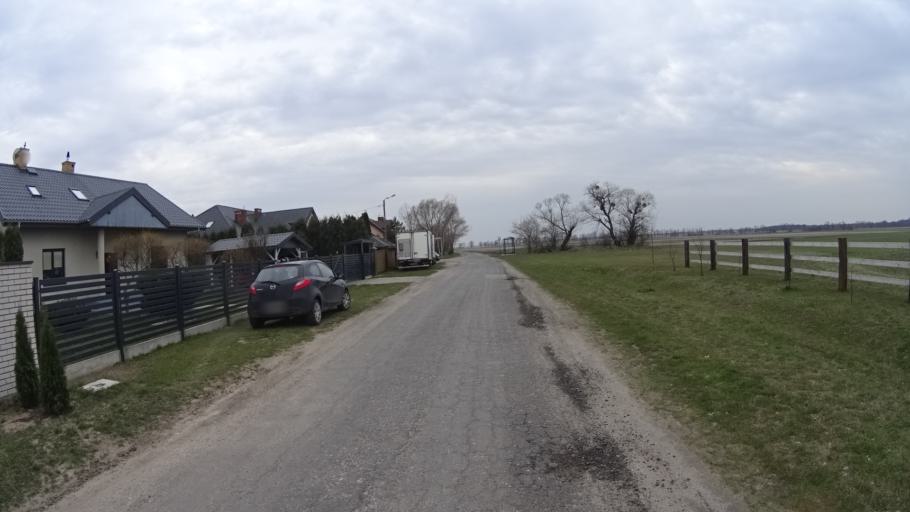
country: PL
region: Masovian Voivodeship
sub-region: Powiat warszawski zachodni
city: Jozefow
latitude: 52.2477
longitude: 20.6613
